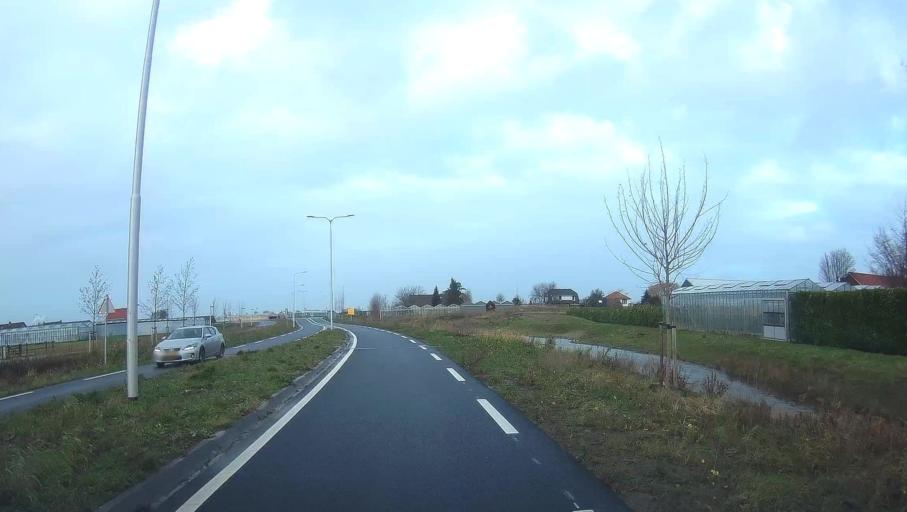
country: NL
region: South Holland
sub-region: Gemeente Pijnacker-Nootdorp
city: Pijnacker
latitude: 52.0129
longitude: 4.4144
